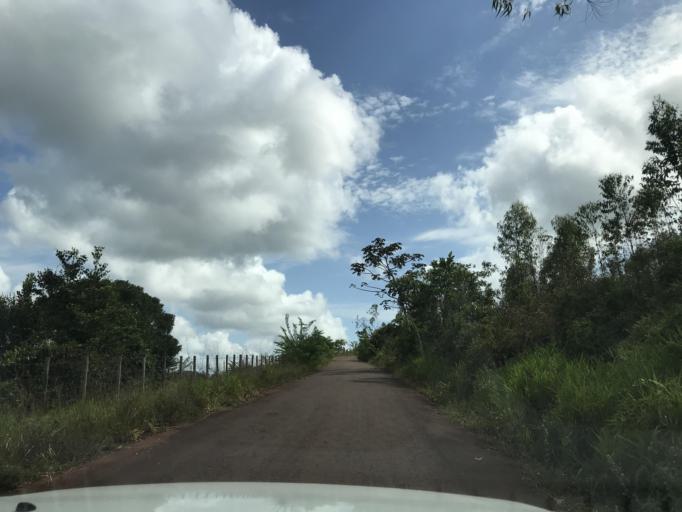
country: BR
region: Bahia
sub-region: Entre Rios
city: Entre Rios
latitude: -12.1732
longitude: -38.1128
